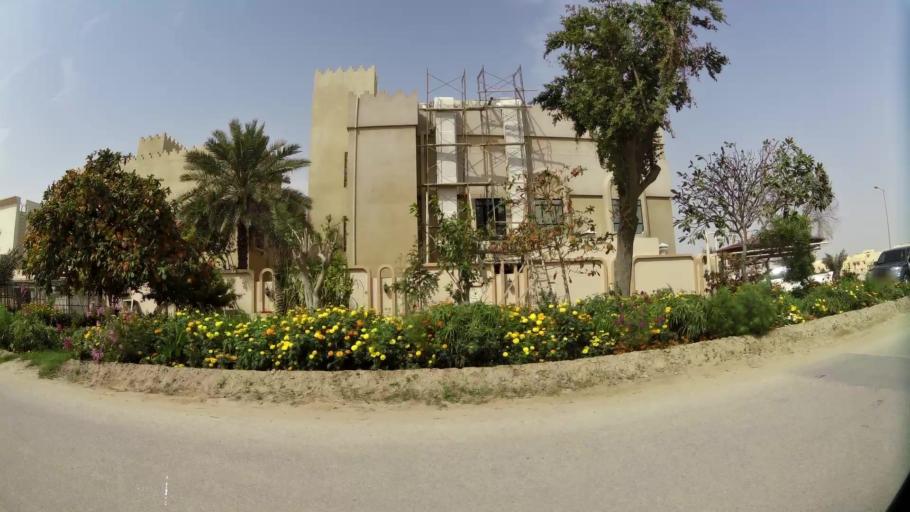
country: QA
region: Baladiyat ad Dawhah
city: Doha
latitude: 25.3008
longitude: 51.4832
